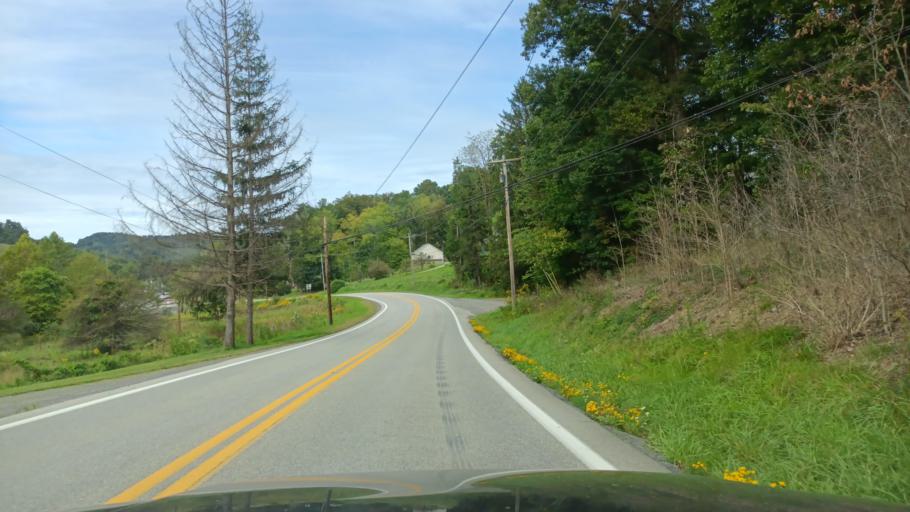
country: US
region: West Virginia
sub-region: Taylor County
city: Grafton
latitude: 39.3282
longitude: -80.1020
